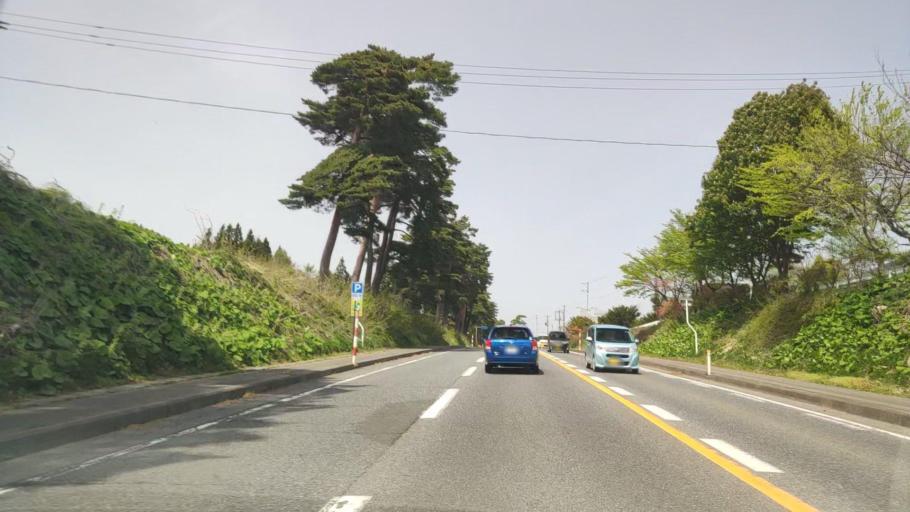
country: JP
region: Aomori
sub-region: Misawa Shi
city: Inuotose
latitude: 40.6678
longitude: 141.1851
